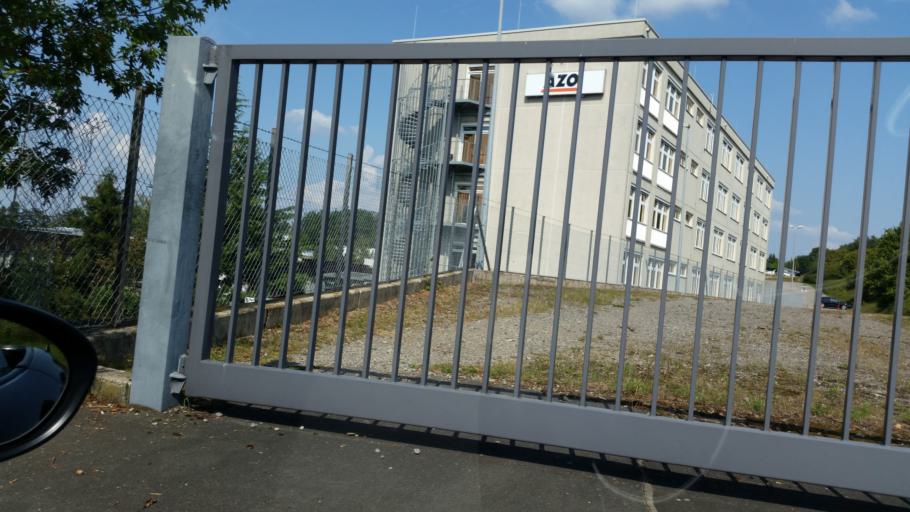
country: DE
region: Baden-Wuerttemberg
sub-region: Karlsruhe Region
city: Osterburken
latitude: 49.4283
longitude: 9.4376
